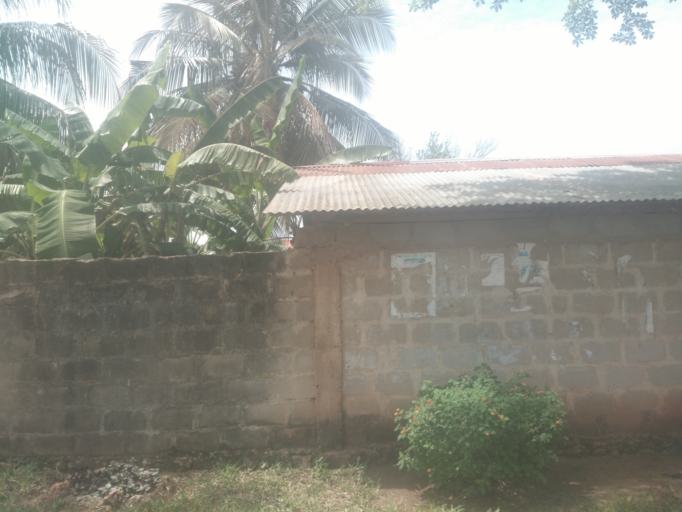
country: TZ
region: Zanzibar Urban/West
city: Zanzibar
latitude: -6.2298
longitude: 39.2183
